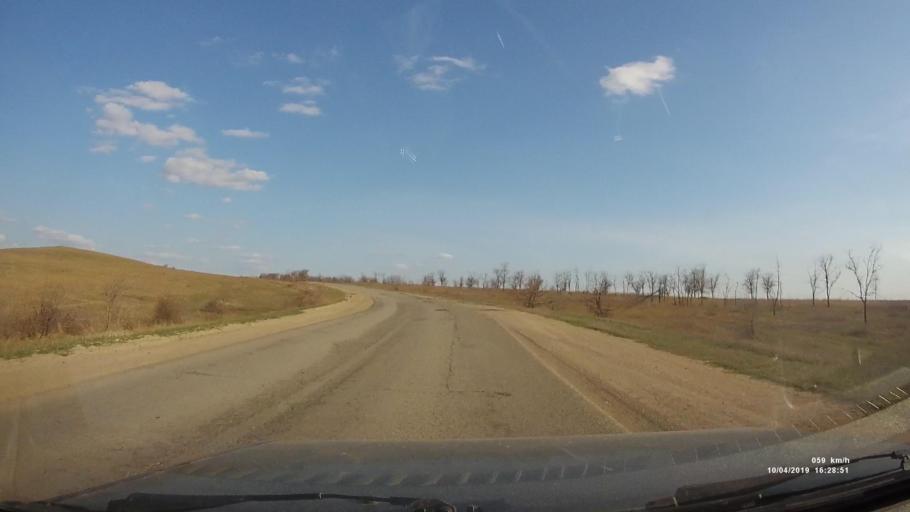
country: RU
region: Rostov
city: Staraya Stanitsa
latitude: 48.2719
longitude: 40.3487
